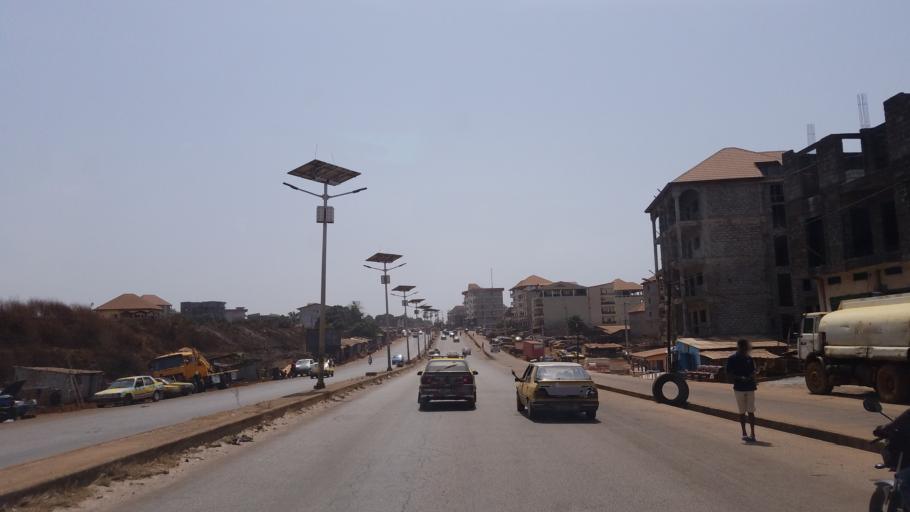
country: GN
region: Conakry
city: Conakry
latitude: 9.6502
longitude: -13.5823
